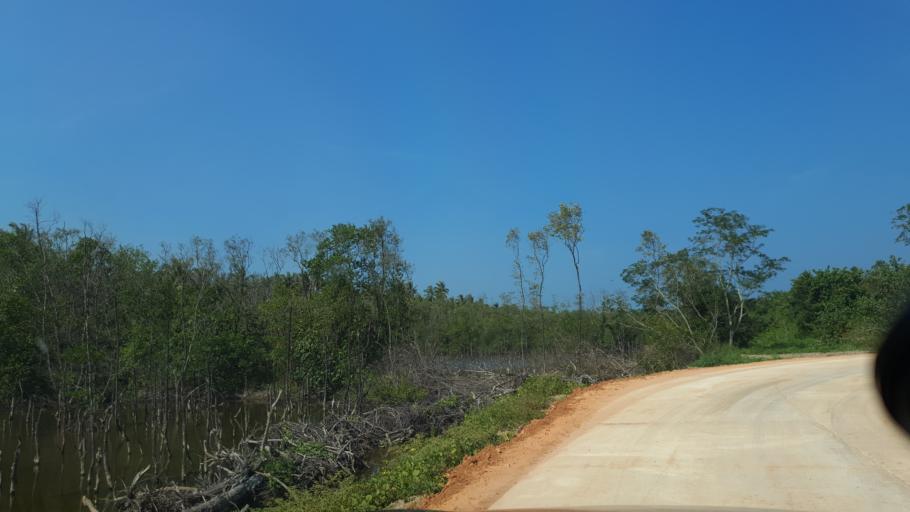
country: TH
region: Surat Thani
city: Tha Chana
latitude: 9.5942
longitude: 99.2078
